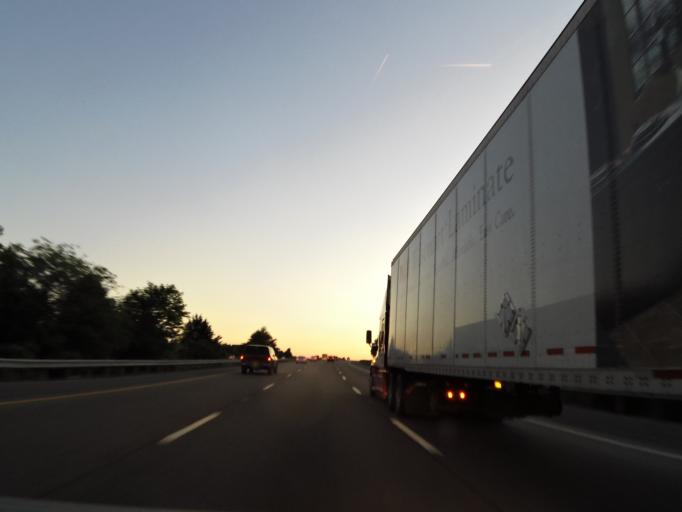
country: US
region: Tennessee
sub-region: Sevier County
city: Sevierville
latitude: 35.9866
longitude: -83.5852
